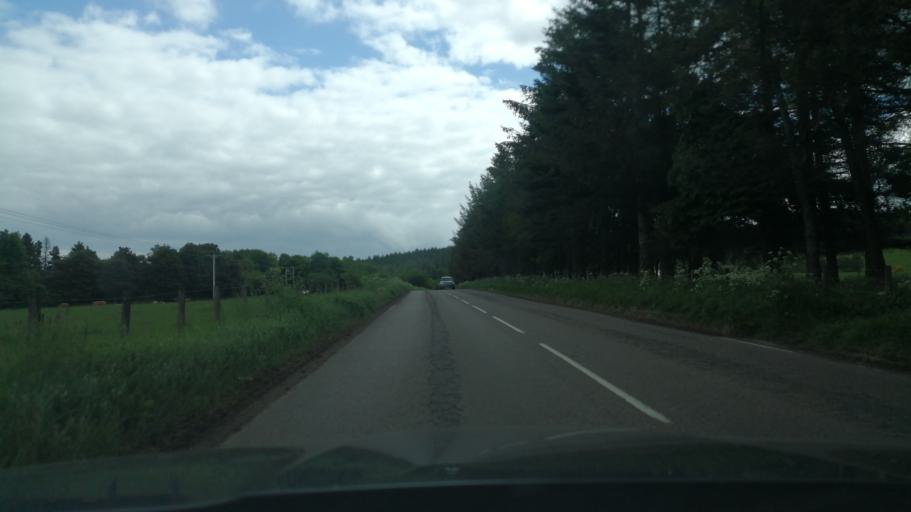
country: GB
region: Scotland
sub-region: Moray
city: Fochabers
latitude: 57.5465
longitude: -3.1224
